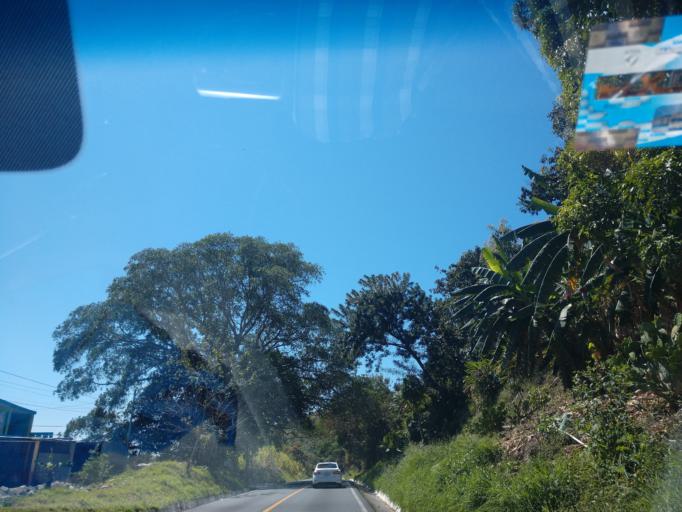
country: MX
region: Nayarit
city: Xalisco
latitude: 21.3989
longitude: -104.8953
